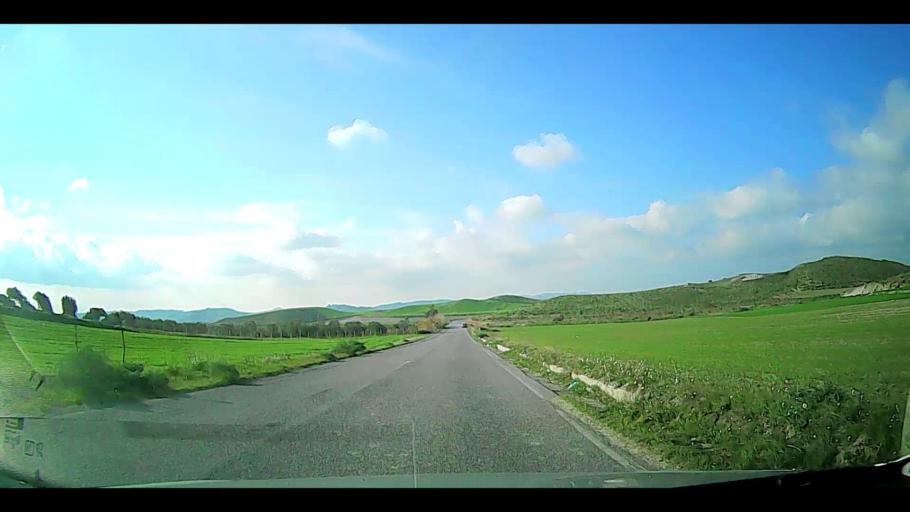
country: IT
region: Calabria
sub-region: Provincia di Crotone
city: Rocca di Neto
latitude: 39.1908
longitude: 17.0582
